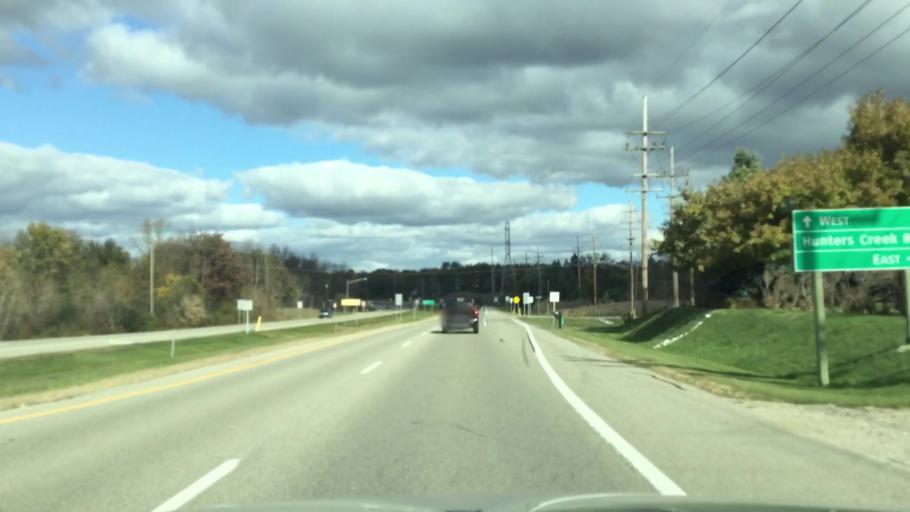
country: US
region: Michigan
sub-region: Lapeer County
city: Lapeer
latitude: 42.9841
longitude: -83.3152
